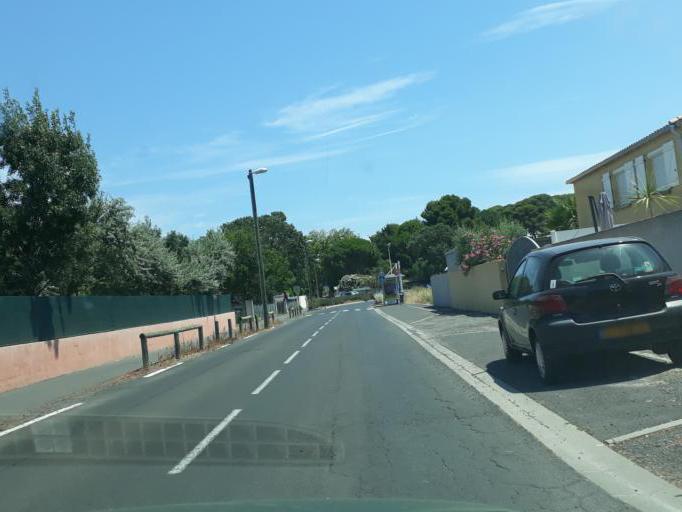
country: FR
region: Languedoc-Roussillon
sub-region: Departement de l'Herault
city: Agde
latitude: 43.2933
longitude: 3.4533
